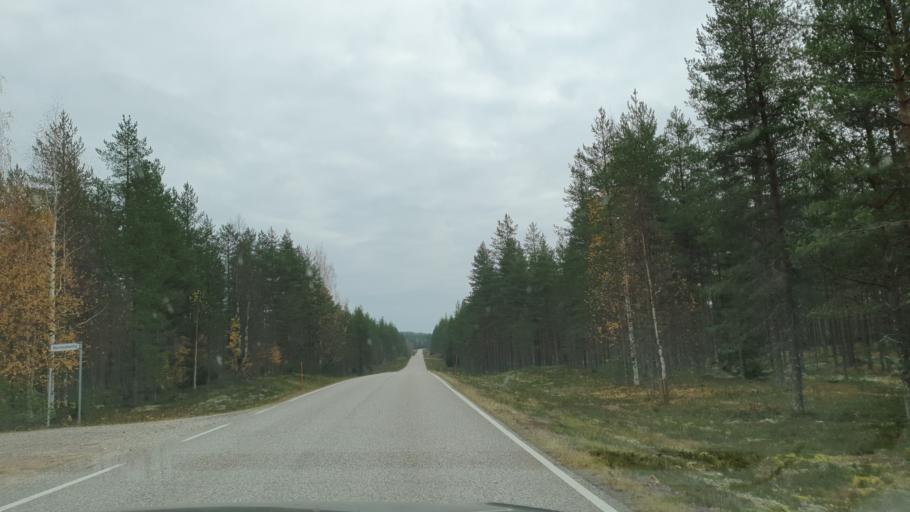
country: FI
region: Kainuu
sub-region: Kajaani
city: Paltamo
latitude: 64.6330
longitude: 27.9844
